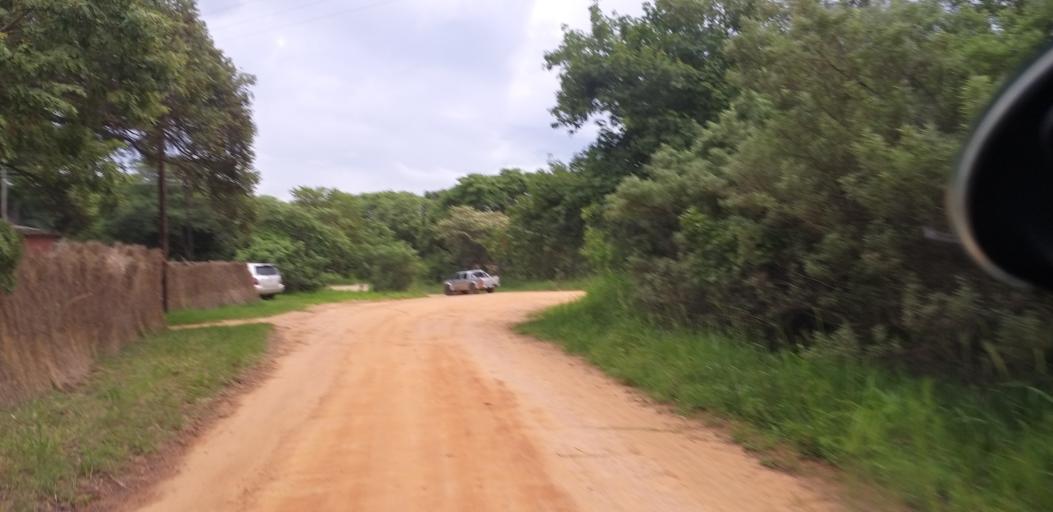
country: ZM
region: Lusaka
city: Chongwe
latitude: -15.1600
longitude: 28.4824
